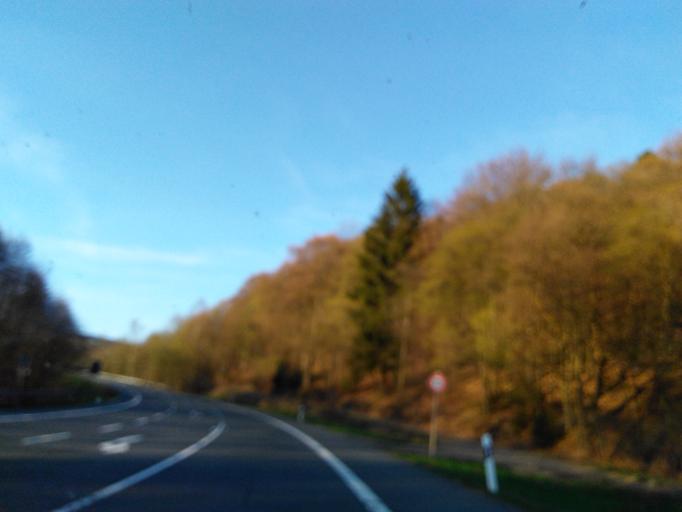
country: DE
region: North Rhine-Westphalia
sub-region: Regierungsbezirk Arnsberg
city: Herscheid
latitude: 51.1085
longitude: 7.7261
